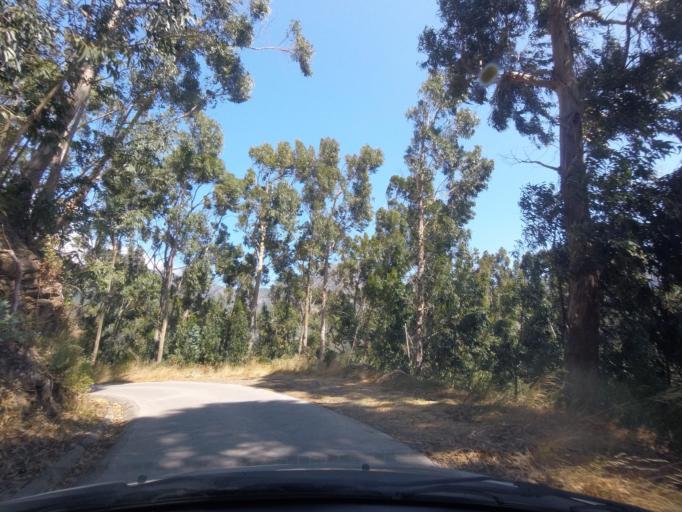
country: PT
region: Madeira
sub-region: Sao Vicente
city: Sao Vicente
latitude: 32.7399
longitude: -17.0274
